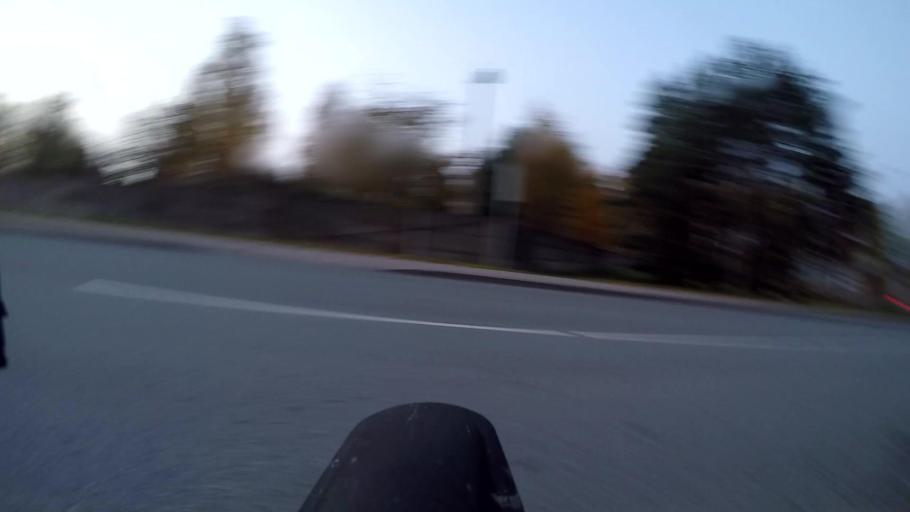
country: LV
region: Marupe
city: Marupe
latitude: 56.9187
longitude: 23.9887
